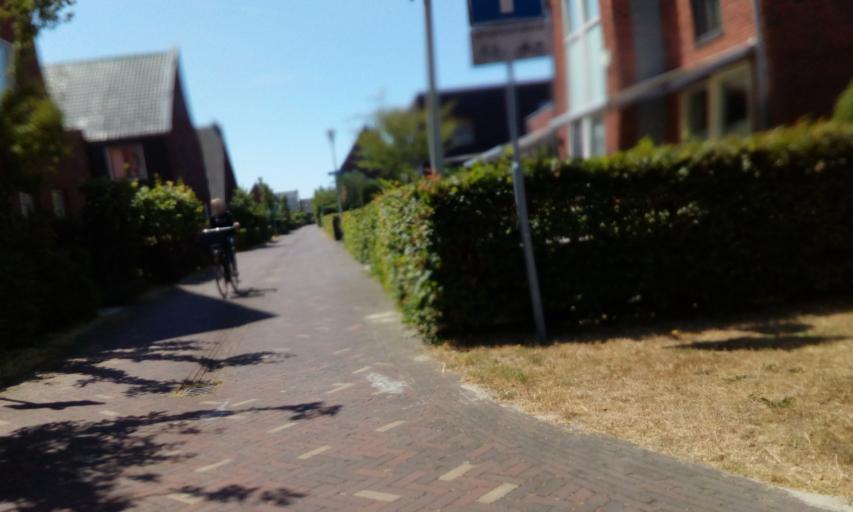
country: NL
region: South Holland
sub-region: Gemeente Den Haag
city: Ypenburg
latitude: 52.0334
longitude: 4.3907
